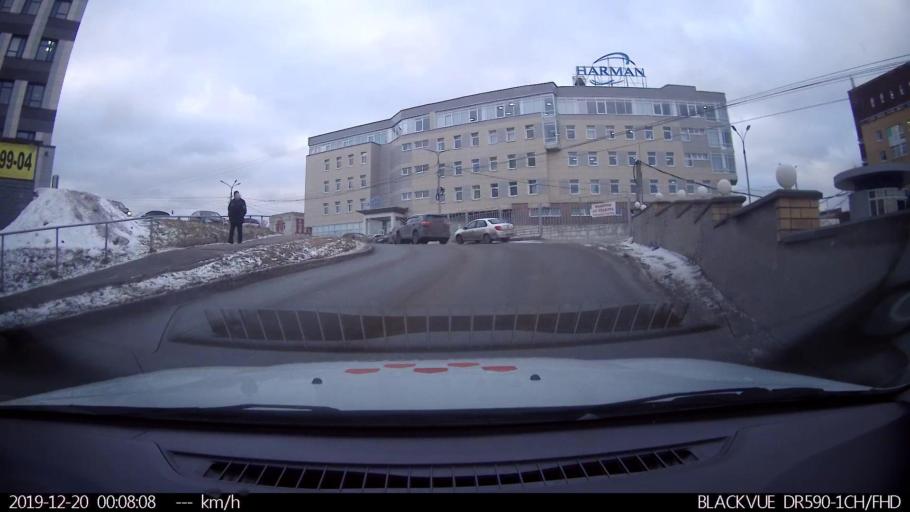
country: RU
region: Jaroslavl
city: Konstantinovskiy
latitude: 57.7831
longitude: 39.7437
